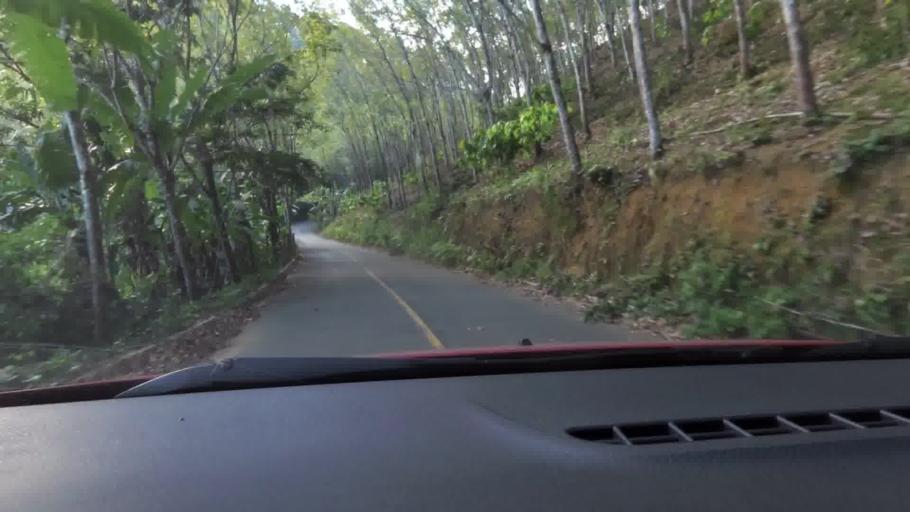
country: BR
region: Espirito Santo
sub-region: Guarapari
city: Guarapari
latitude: -20.5833
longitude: -40.5641
